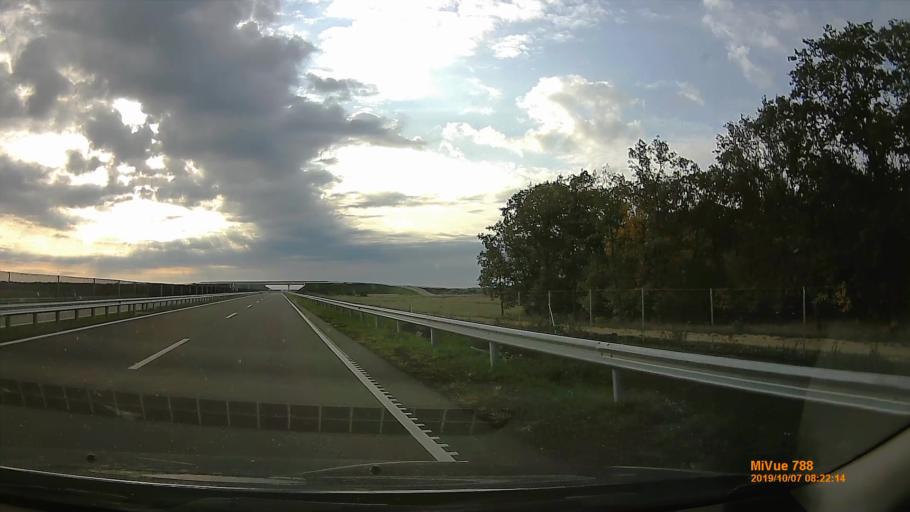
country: HU
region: Jasz-Nagykun-Szolnok
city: Kunszentmarton
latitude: 46.8557
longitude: 20.3111
